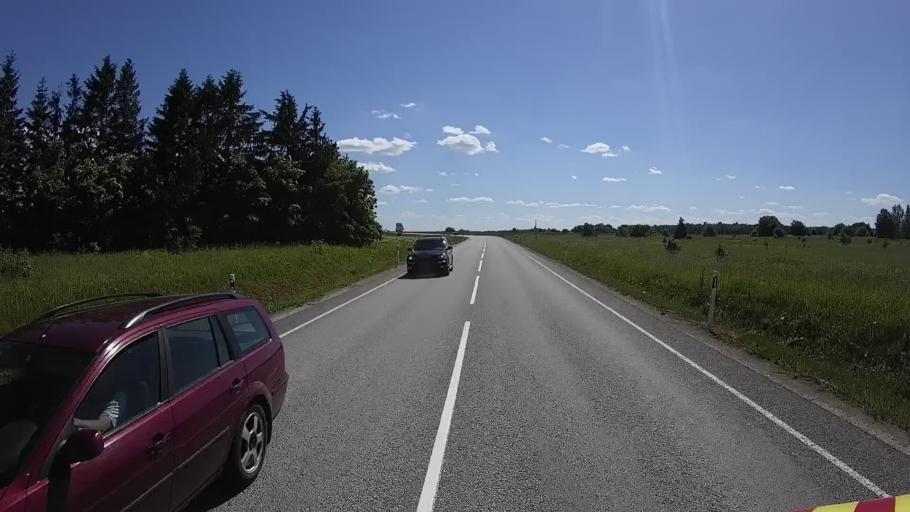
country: EE
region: Ida-Virumaa
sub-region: Johvi vald
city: Johvi
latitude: 59.3770
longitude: 27.3509
